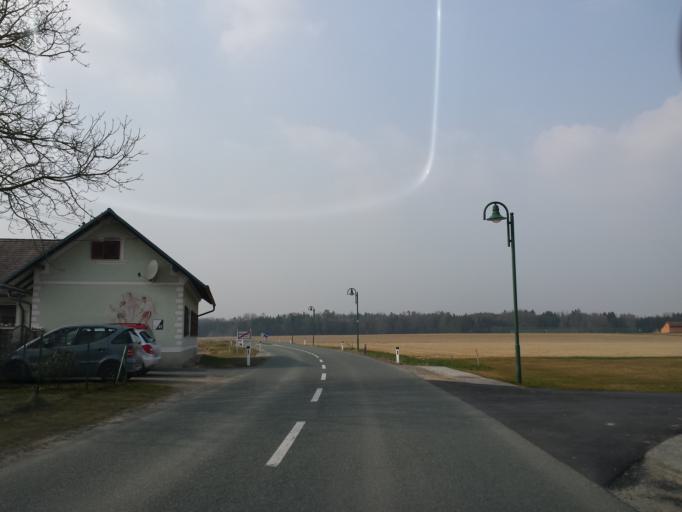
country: AT
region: Burgenland
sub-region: Politischer Bezirk Jennersdorf
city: Konigsdorf
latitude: 47.0000
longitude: 16.1361
